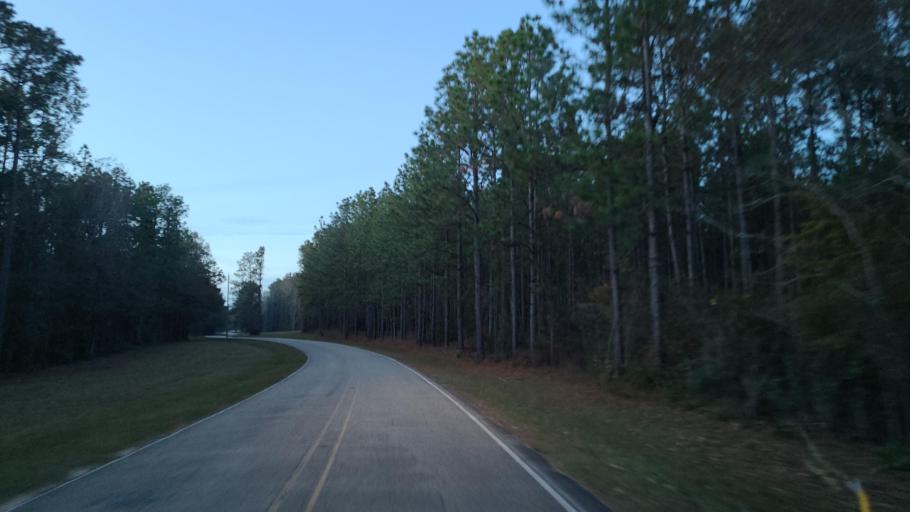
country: US
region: Mississippi
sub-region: Perry County
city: New Augusta
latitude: 31.1500
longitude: -89.2046
